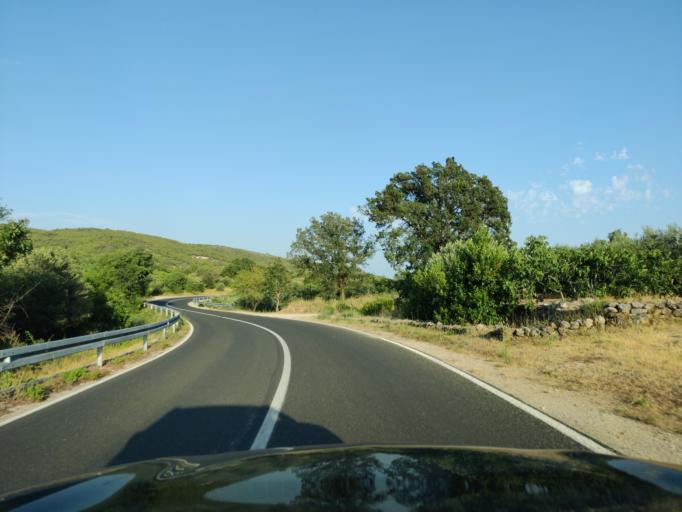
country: HR
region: Sibensko-Kniniska
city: Tribunj
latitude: 43.7748
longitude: 15.7220
